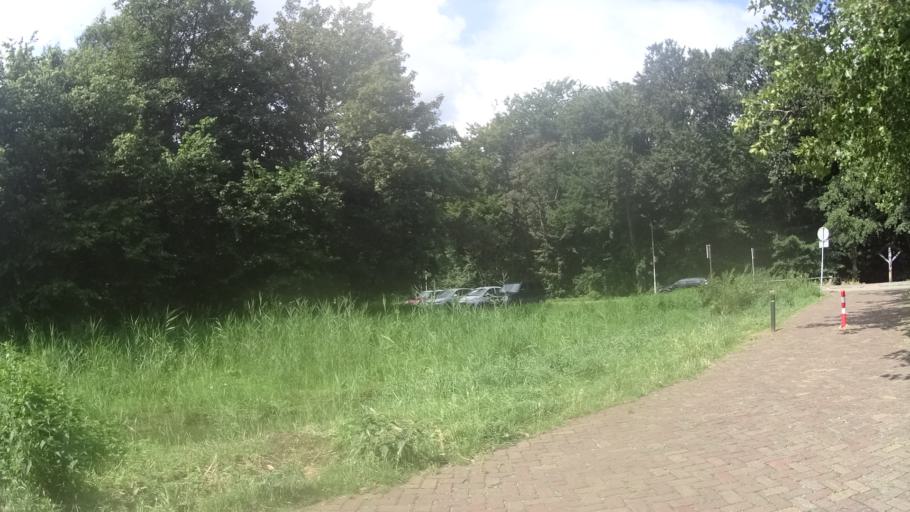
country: NL
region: North Holland
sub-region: Gemeente Beverwijk
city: Beverwijk
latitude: 52.4822
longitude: 4.6416
